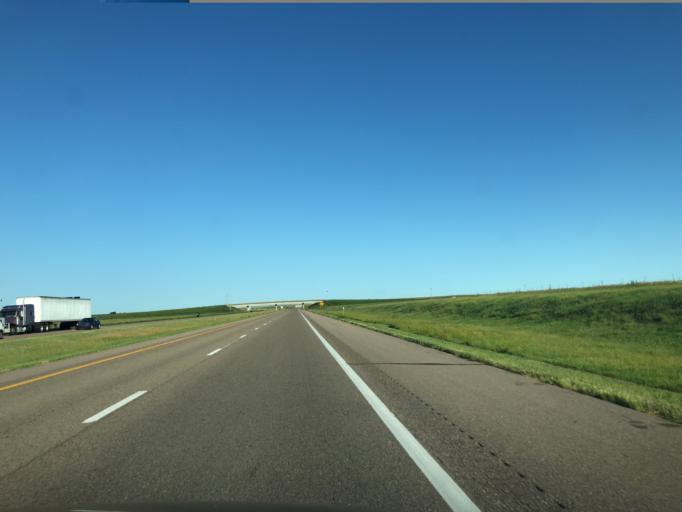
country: US
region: Kansas
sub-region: Trego County
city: WaKeeney
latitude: 39.0213
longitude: -99.9219
